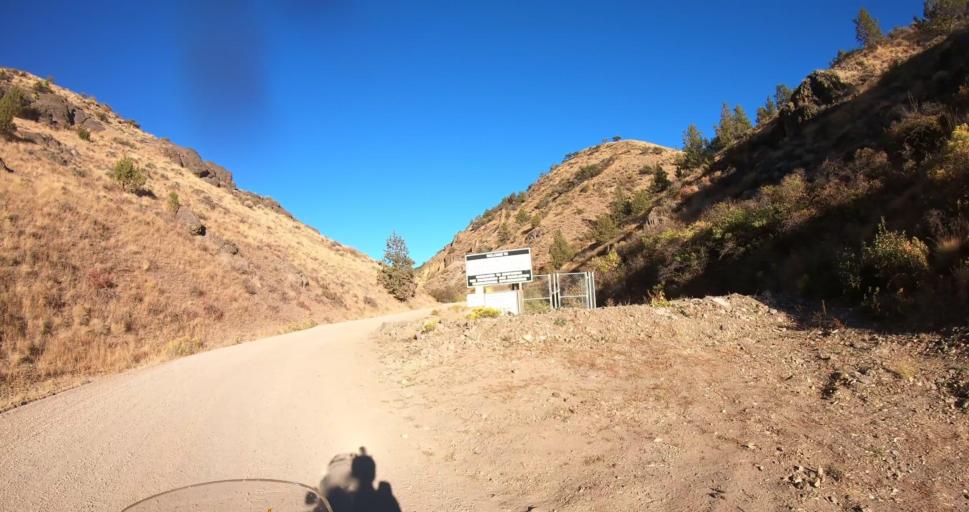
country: US
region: Oregon
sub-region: Lake County
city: Lakeview
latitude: 42.1899
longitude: -120.3416
